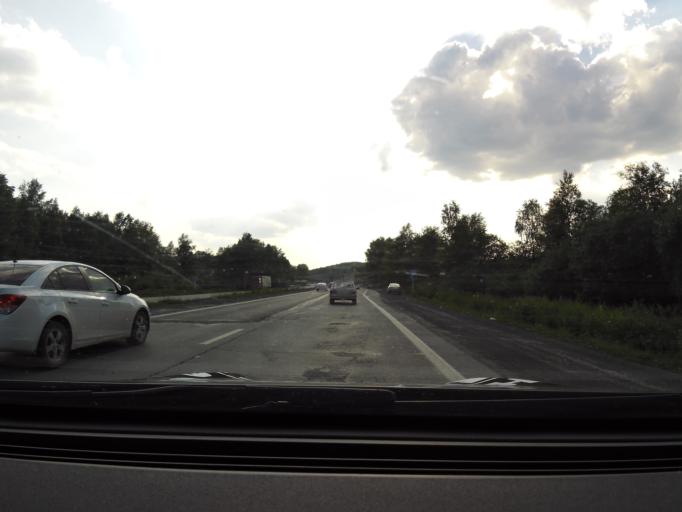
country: RU
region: Sverdlovsk
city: Severka
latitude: 56.8448
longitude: 60.2217
